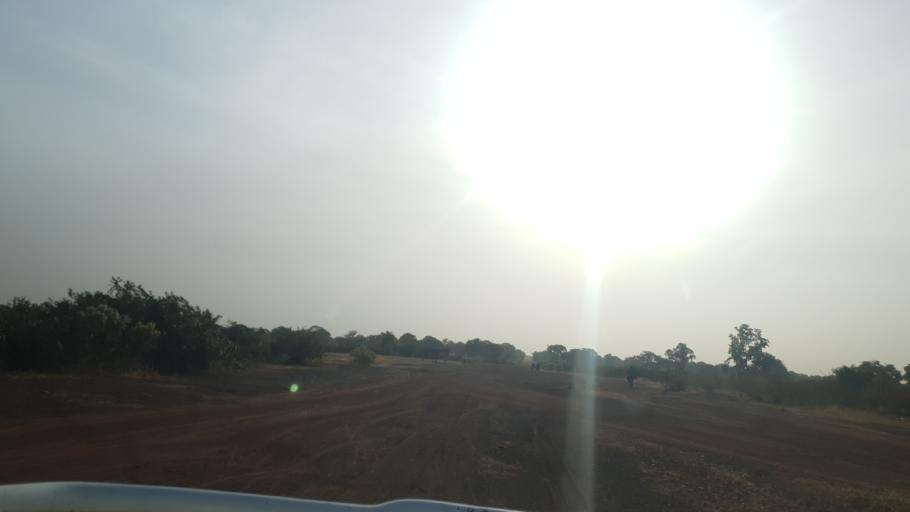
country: ML
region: Koulikoro
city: Dioila
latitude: 12.7641
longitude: -6.9133
